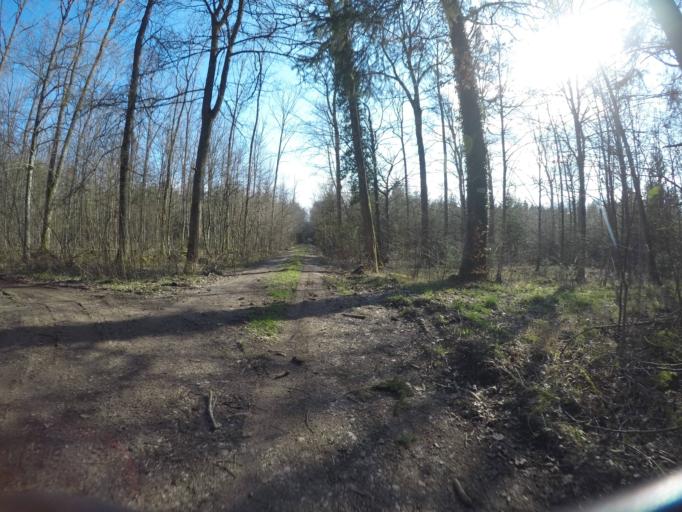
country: DE
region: Baden-Wuerttemberg
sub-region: Tuebingen Region
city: Dusslingen
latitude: 48.4652
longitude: 9.0265
